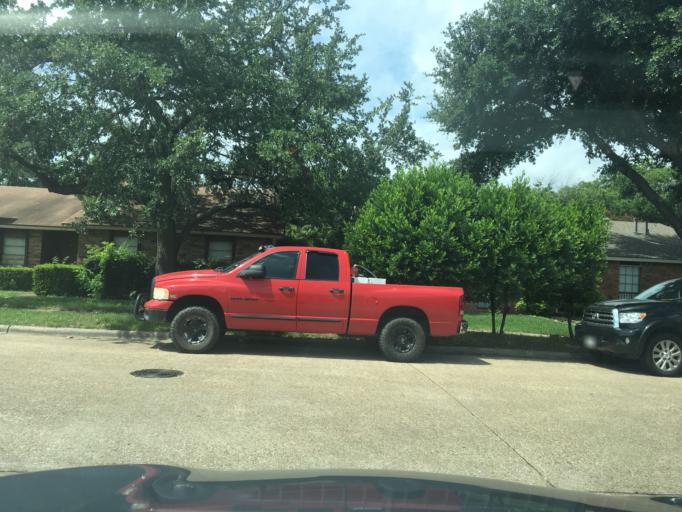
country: US
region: Texas
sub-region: Dallas County
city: Richardson
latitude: 32.9126
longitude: -96.7066
